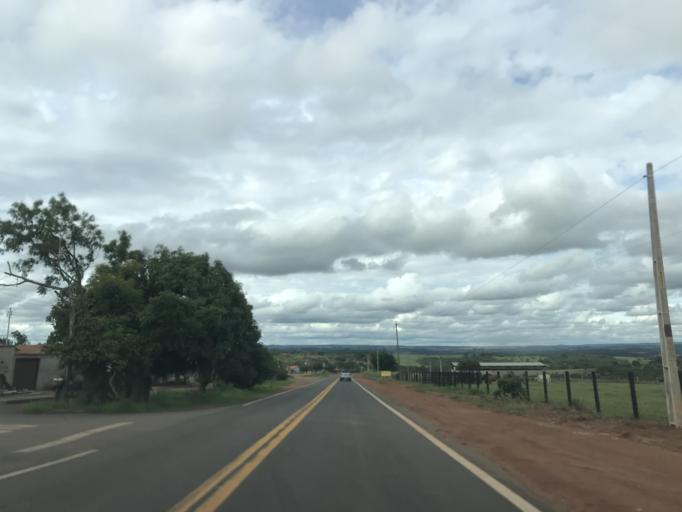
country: BR
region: Goias
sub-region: Piracanjuba
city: Piracanjuba
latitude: -17.2045
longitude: -48.7046
